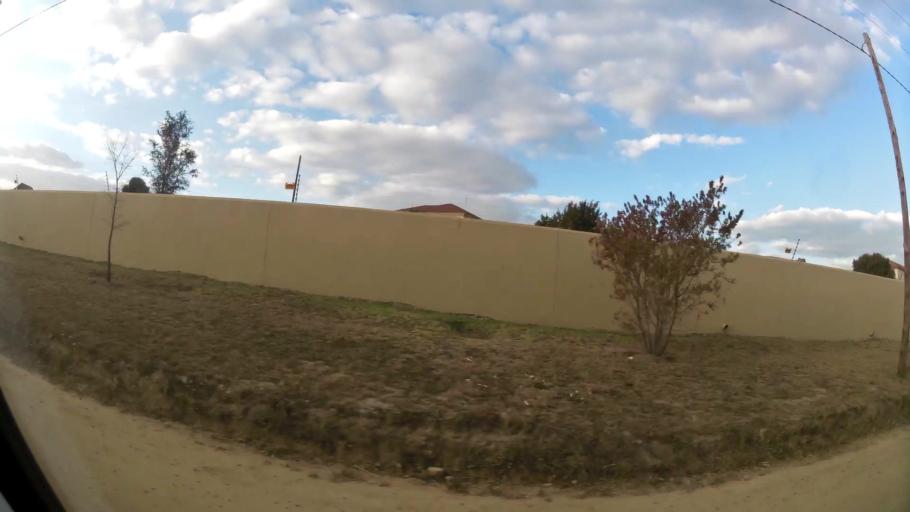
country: ZA
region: Gauteng
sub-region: City of Johannesburg Metropolitan Municipality
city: Diepsloot
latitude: -26.0042
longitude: 27.9696
